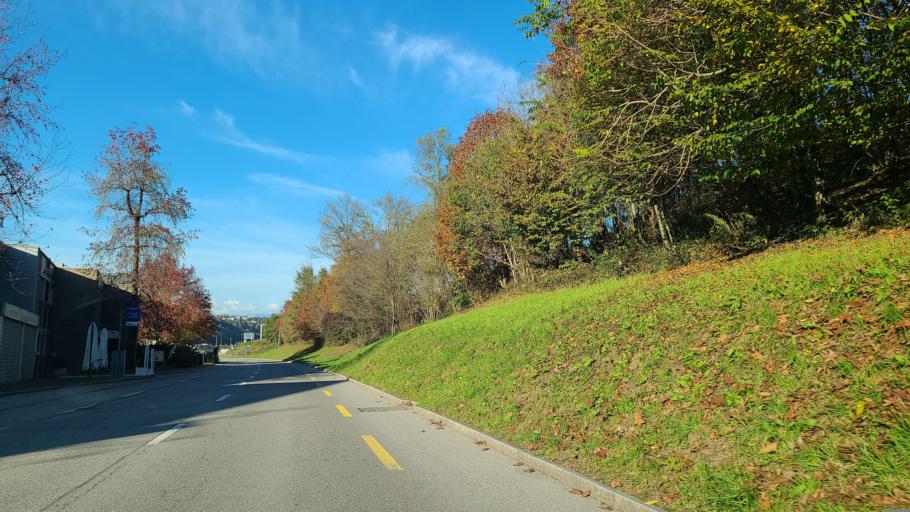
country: CH
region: Ticino
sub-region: Lugano District
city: Montagnola
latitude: 45.9638
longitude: 8.9255
